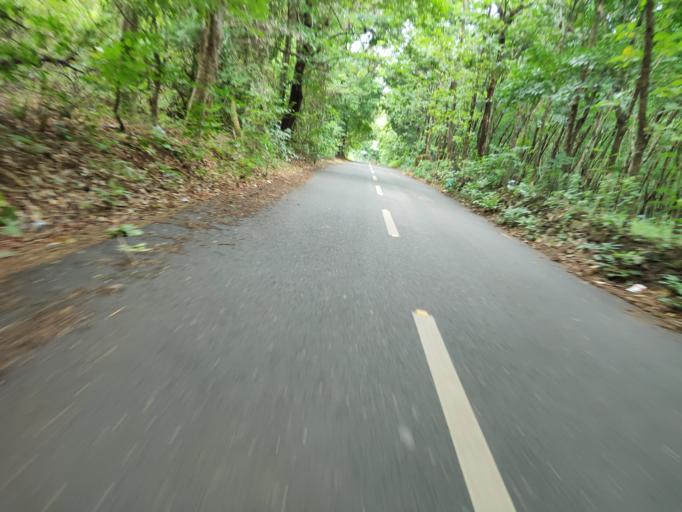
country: IN
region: Kerala
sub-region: Malappuram
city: Manjeri
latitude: 11.2232
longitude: 76.2507
